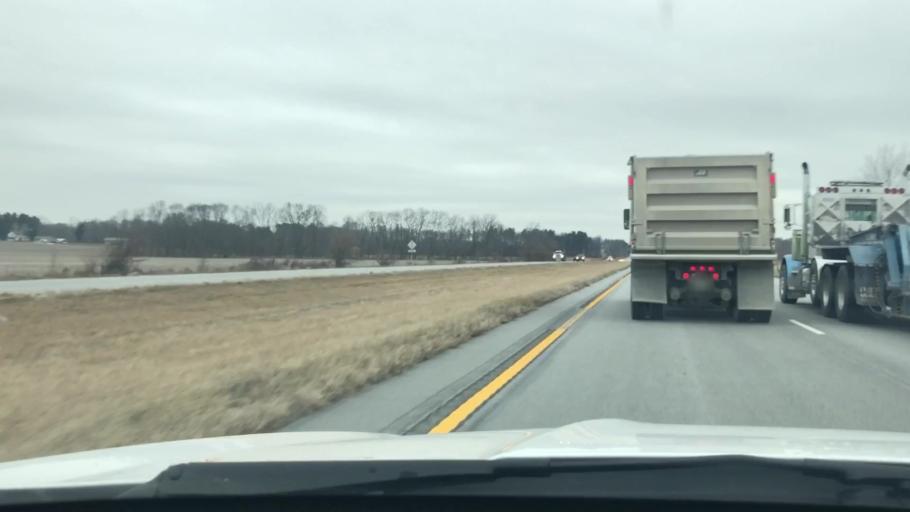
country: US
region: Indiana
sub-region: Miami County
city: Peru
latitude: 40.8246
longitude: -86.1294
